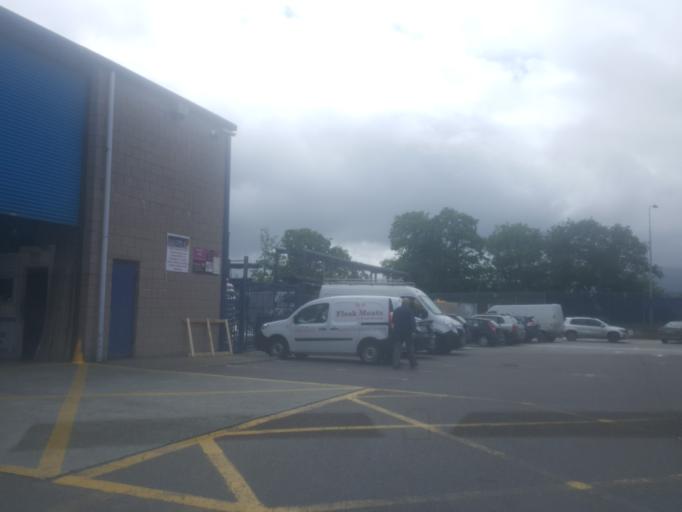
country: IE
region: Munster
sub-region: Ciarrai
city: Cill Airne
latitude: 52.0628
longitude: -9.4816
